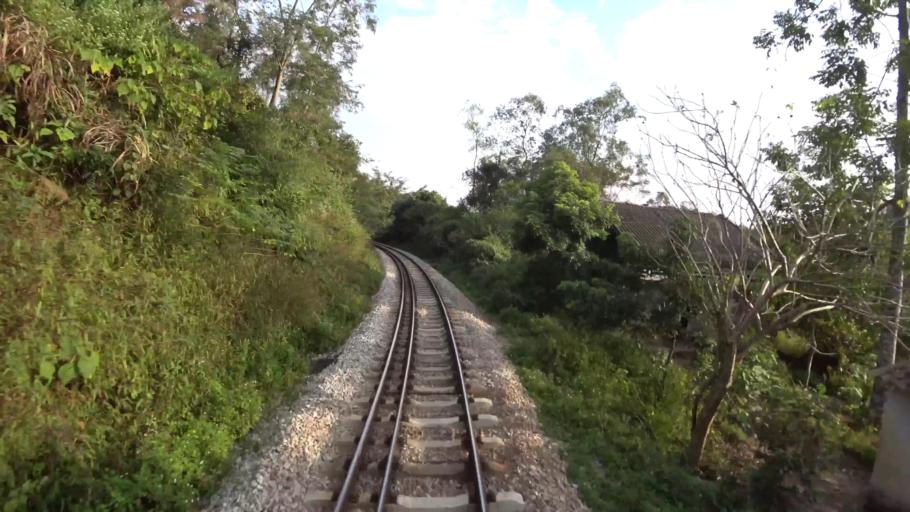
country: VN
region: Lang Son
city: Thi Tran Cao Loc
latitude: 21.9308
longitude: 106.7004
